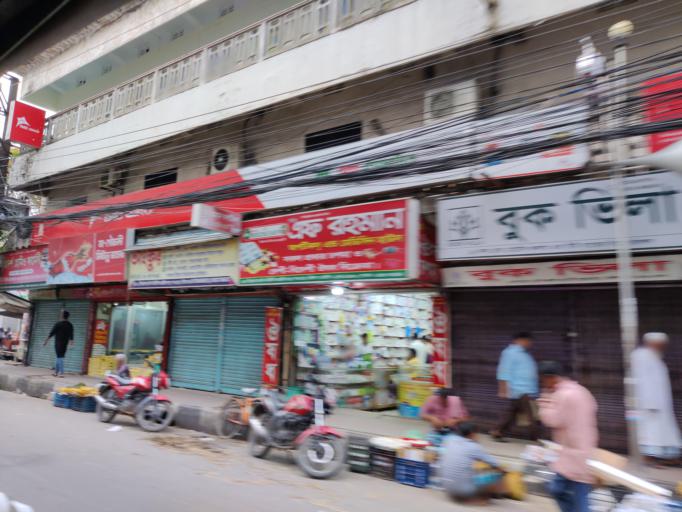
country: BD
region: Barisal
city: Barisal
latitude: 22.7043
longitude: 90.3706
